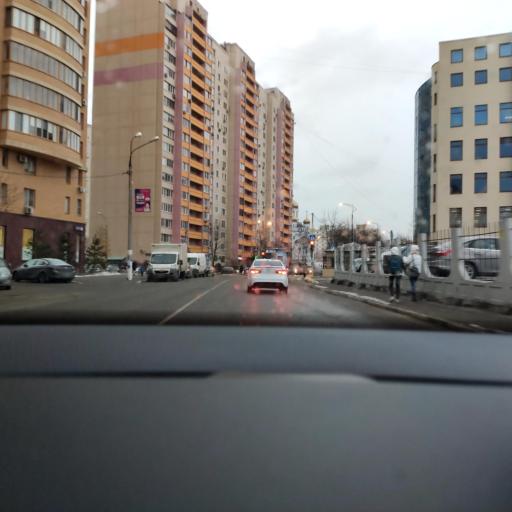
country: RU
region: Moskovskaya
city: Reutov
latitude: 55.7576
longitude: 37.8621
